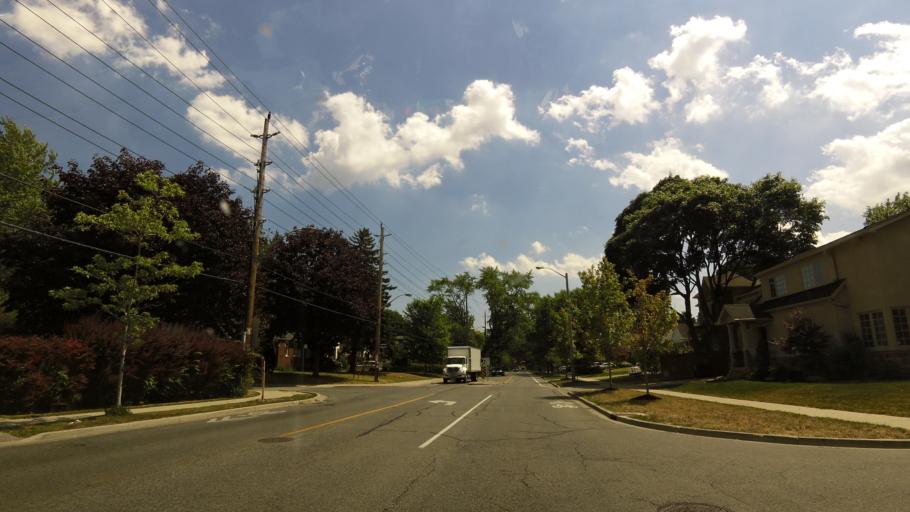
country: CA
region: Ontario
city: Etobicoke
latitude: 43.6560
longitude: -79.5152
